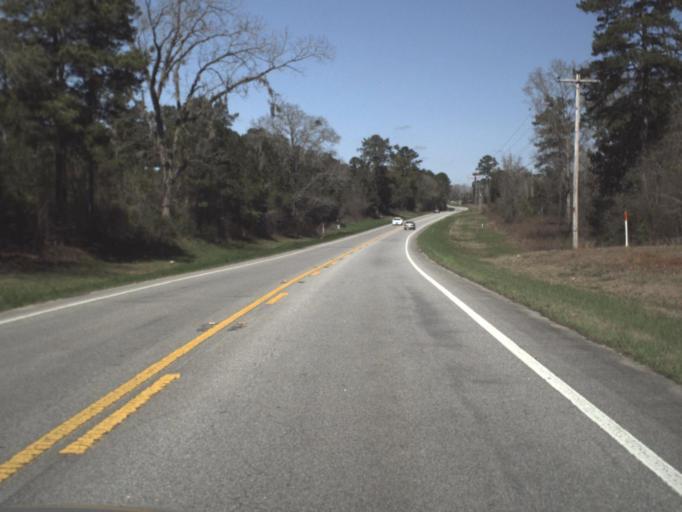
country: US
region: Florida
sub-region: Gadsden County
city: Quincy
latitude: 30.6353
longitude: -84.5996
